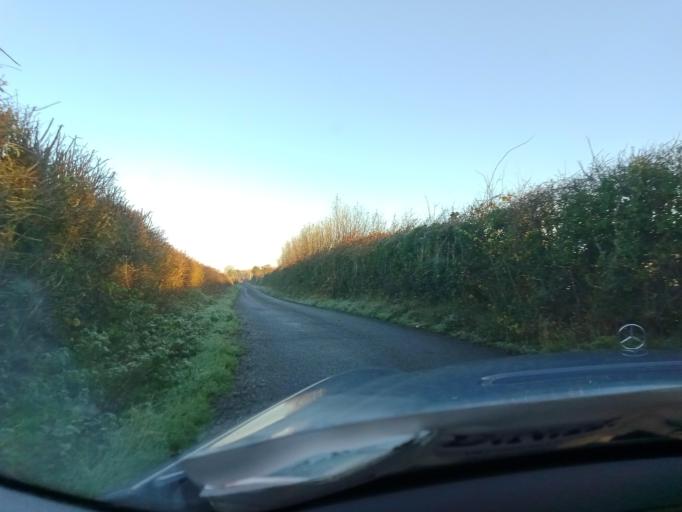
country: IE
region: Leinster
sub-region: Kilkenny
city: Callan
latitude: 52.5163
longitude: -7.4468
